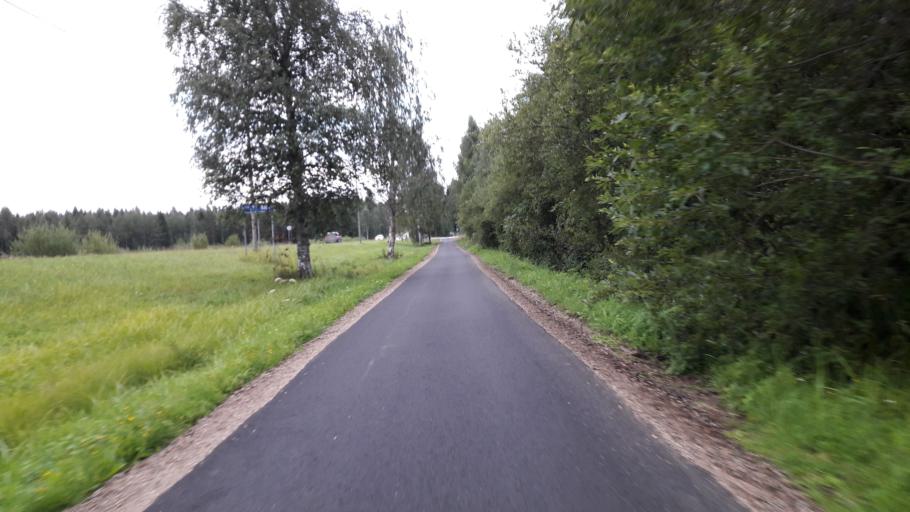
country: FI
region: North Karelia
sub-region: Joensuu
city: Joensuu
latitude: 62.5317
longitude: 29.8508
